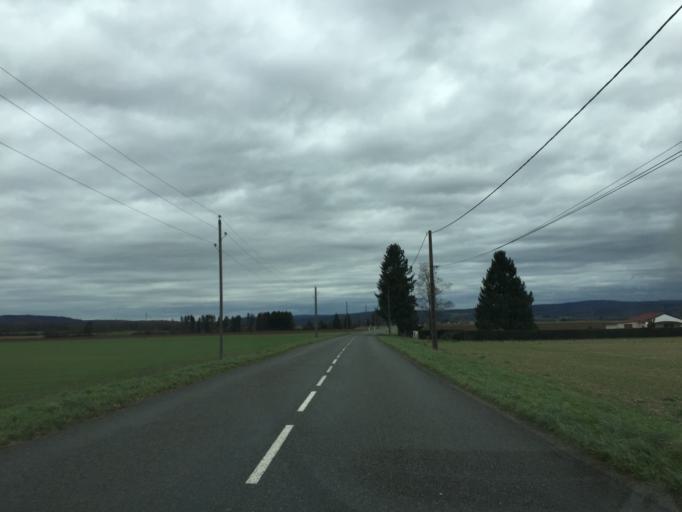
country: FR
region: Franche-Comte
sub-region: Departement du Doubs
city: Arc-et-Senans
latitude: 47.0262
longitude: 5.7335
